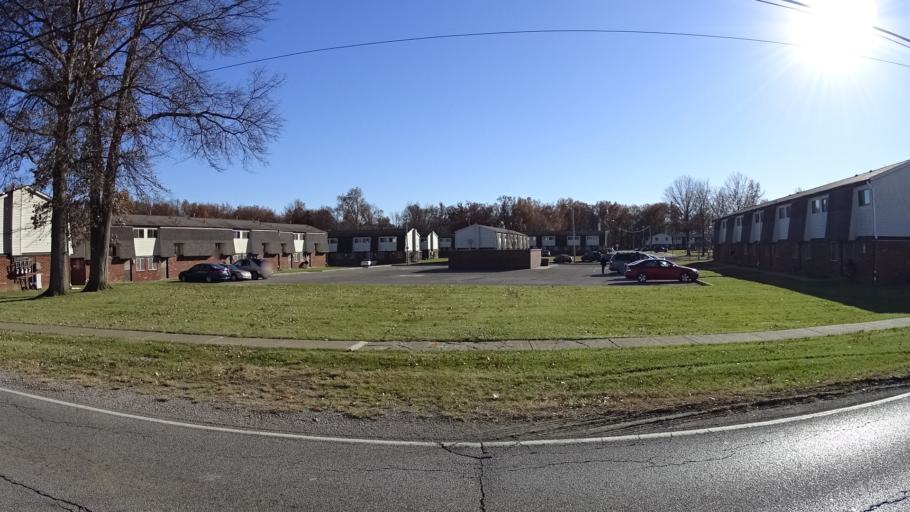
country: US
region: Ohio
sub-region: Lorain County
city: Elyria
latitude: 41.3455
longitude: -82.1000
